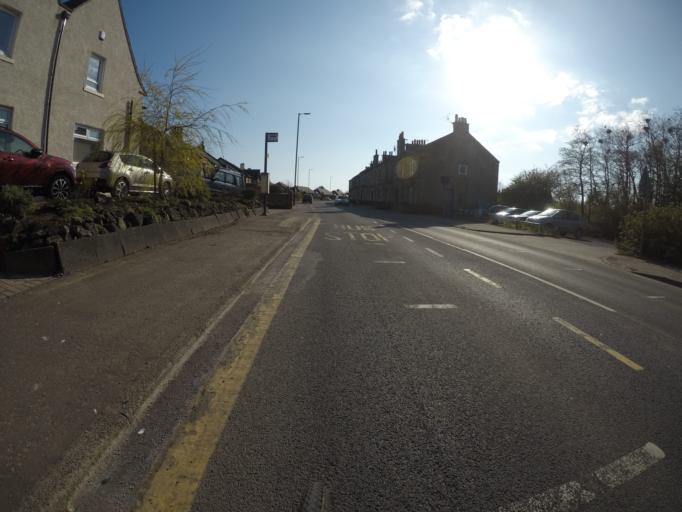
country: GB
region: Scotland
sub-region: North Ayrshire
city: Kilwinning
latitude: 55.6532
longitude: -4.7148
